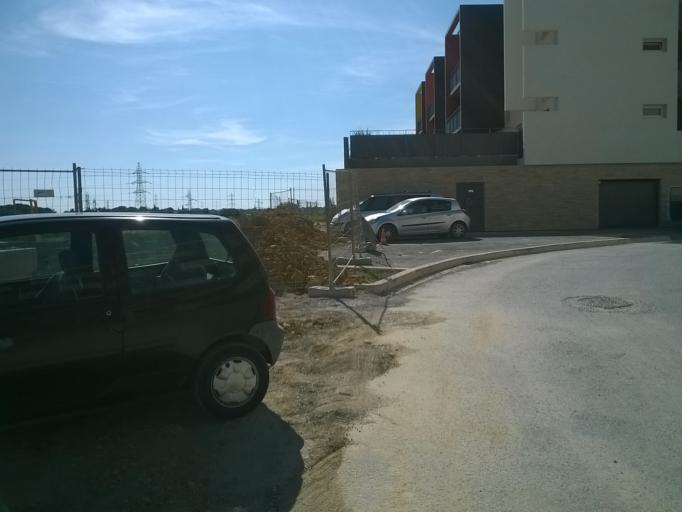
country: FR
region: Languedoc-Roussillon
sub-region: Departement de l'Herault
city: Saint-Jean-de-Vedas
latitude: 43.5807
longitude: 3.8570
